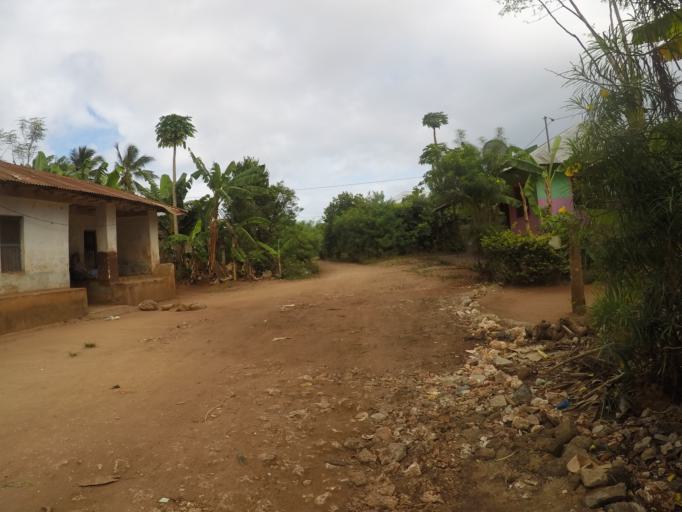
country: TZ
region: Zanzibar Urban/West
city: Zanzibar
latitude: -6.2128
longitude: 39.2160
